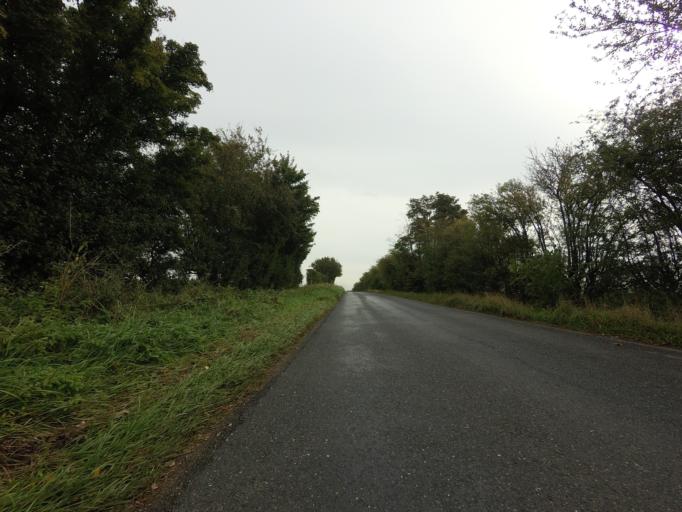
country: GB
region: England
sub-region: Hertfordshire
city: Reed
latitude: 51.9932
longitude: 0.0239
